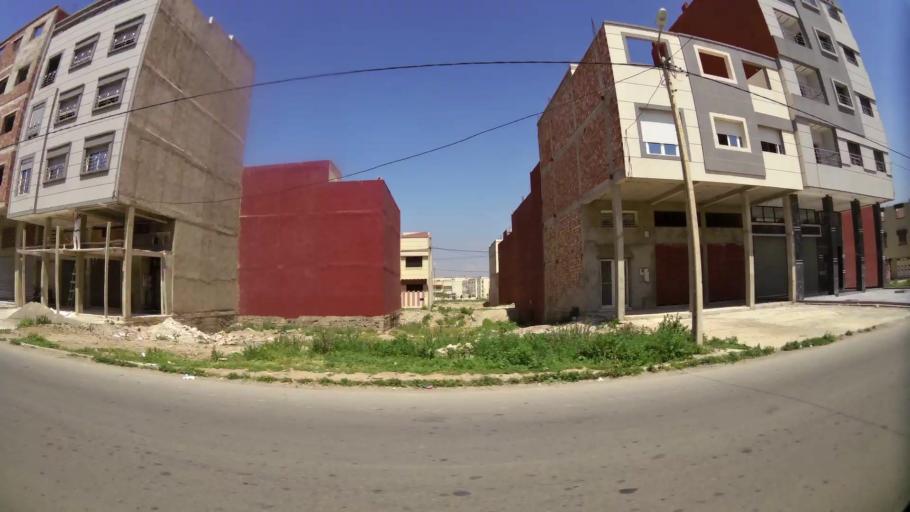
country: MA
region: Oriental
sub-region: Oujda-Angad
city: Oujda
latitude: 34.6976
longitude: -1.8834
